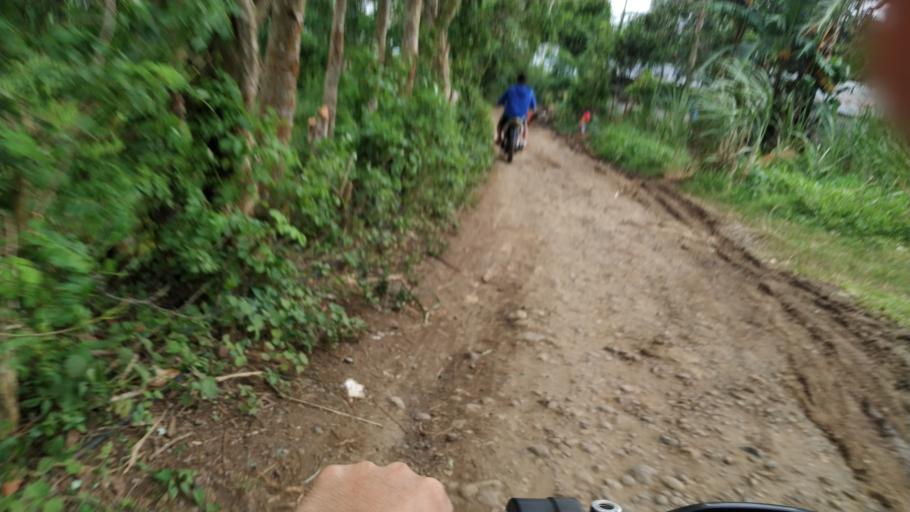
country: PH
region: Western Visayas
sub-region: Province of Negros Occidental
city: Quezon
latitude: 10.4249
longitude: 123.2349
